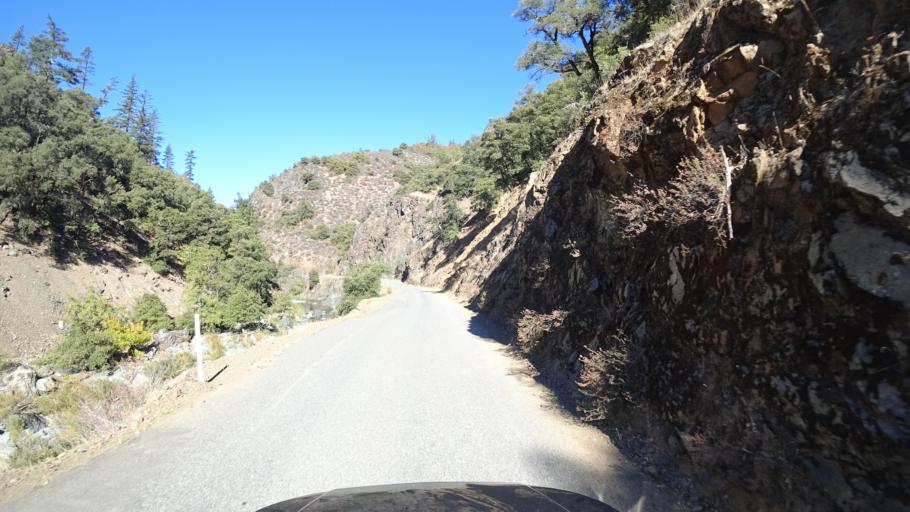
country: US
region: California
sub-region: Humboldt County
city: Willow Creek
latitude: 41.2025
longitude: -123.2236
